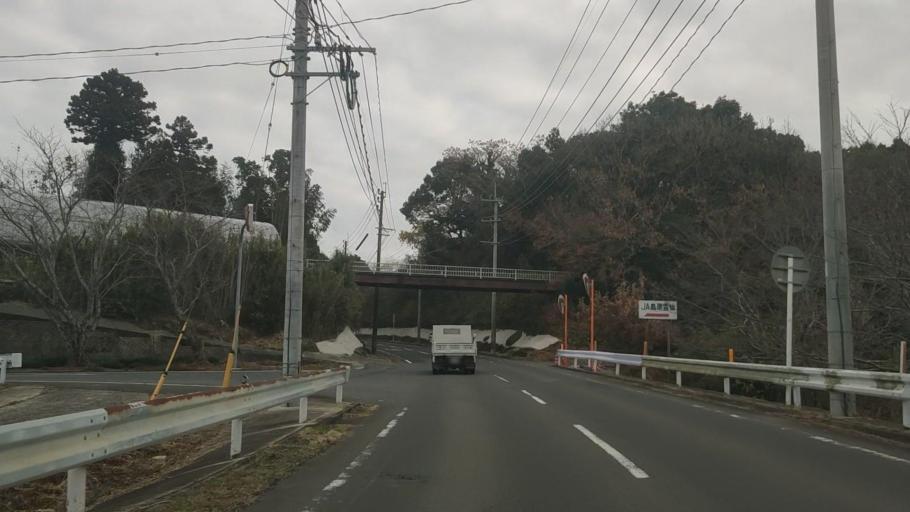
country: JP
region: Nagasaki
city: Shimabara
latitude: 32.8490
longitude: 130.2788
